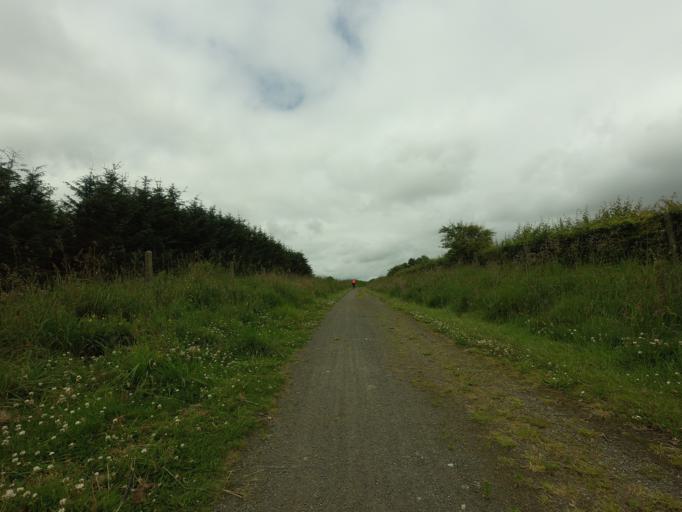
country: GB
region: Scotland
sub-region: Aberdeenshire
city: Mintlaw
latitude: 57.4979
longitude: -2.1406
